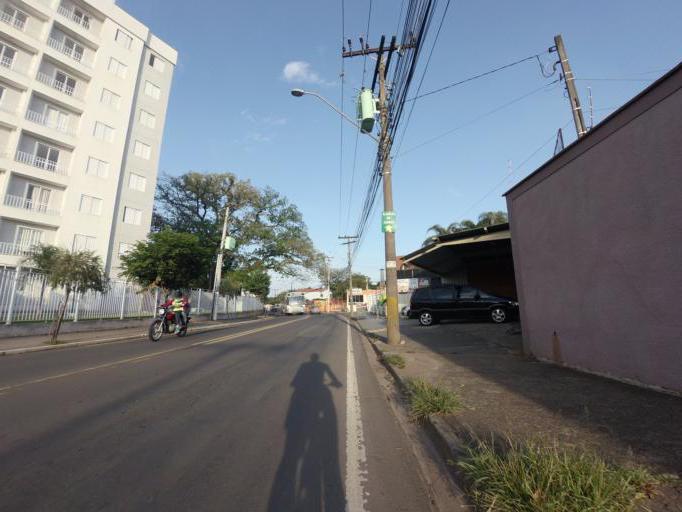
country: BR
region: Sao Paulo
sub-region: Piracicaba
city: Piracicaba
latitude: -22.7411
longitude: -47.6060
